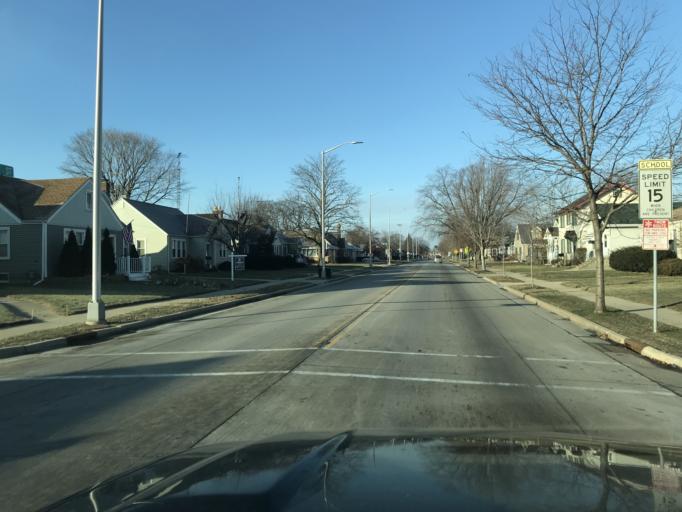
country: US
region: Wisconsin
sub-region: Kenosha County
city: Kenosha
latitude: 42.5661
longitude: -87.8471
